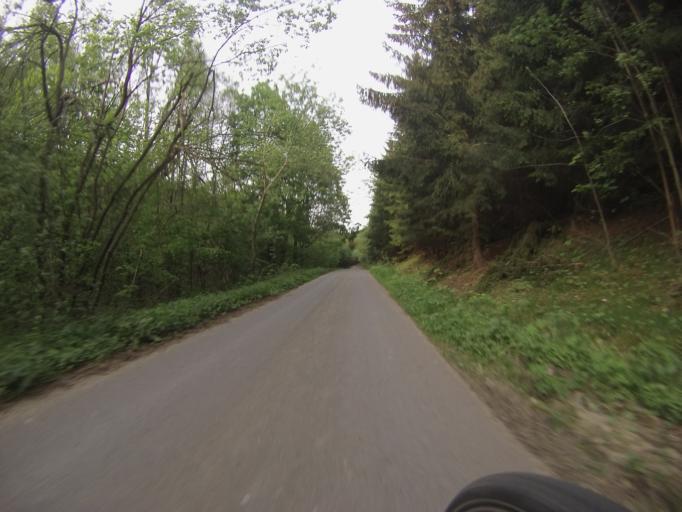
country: CZ
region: Olomoucky
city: Protivanov
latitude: 49.4701
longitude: 16.8810
